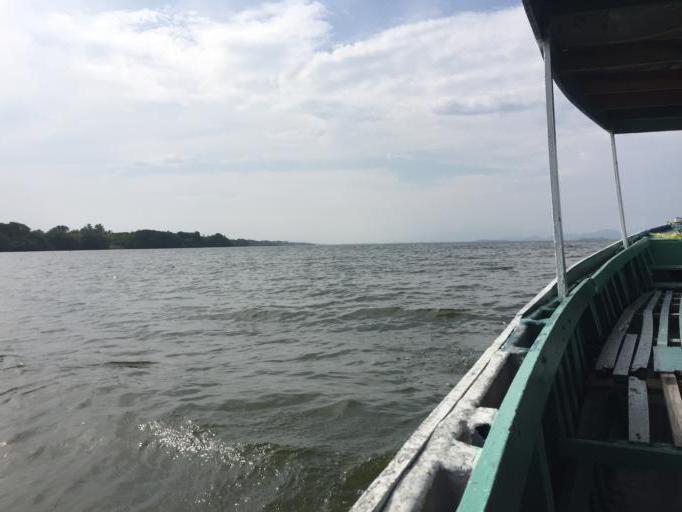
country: MX
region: Guerrero
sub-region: Coyuca de Benitez
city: Colonia Luces en el Mar
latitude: 16.9124
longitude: -99.9778
